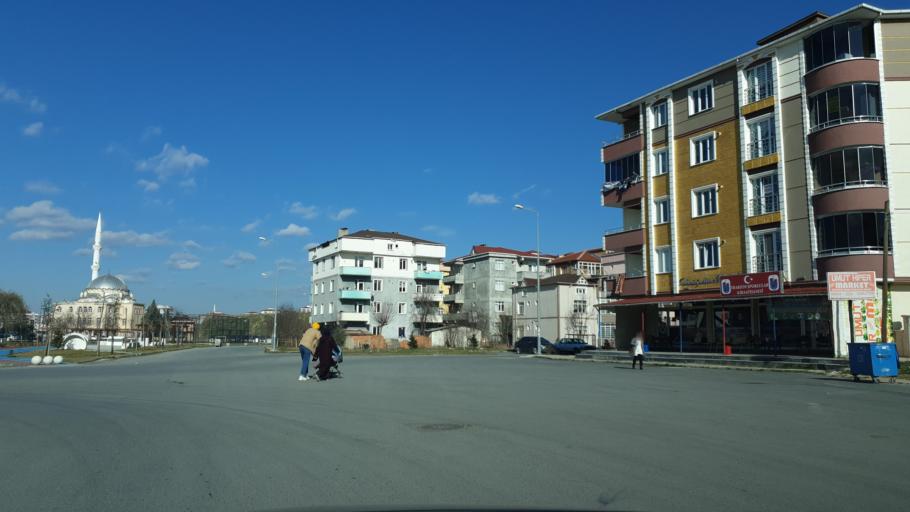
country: TR
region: Tekirdag
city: Cerkezkoey
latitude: 41.2874
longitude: 28.0069
